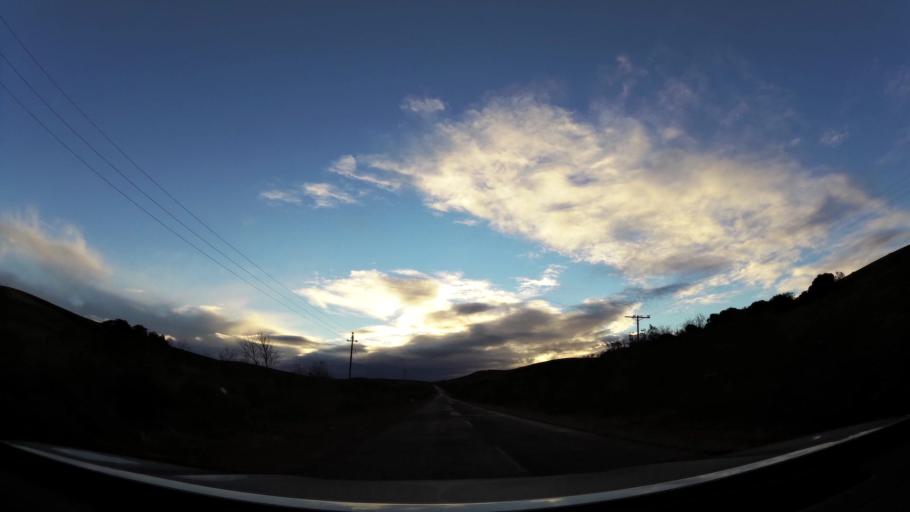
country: ZA
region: Western Cape
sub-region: Eden District Municipality
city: Riversdale
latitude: -34.0592
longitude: 20.8733
